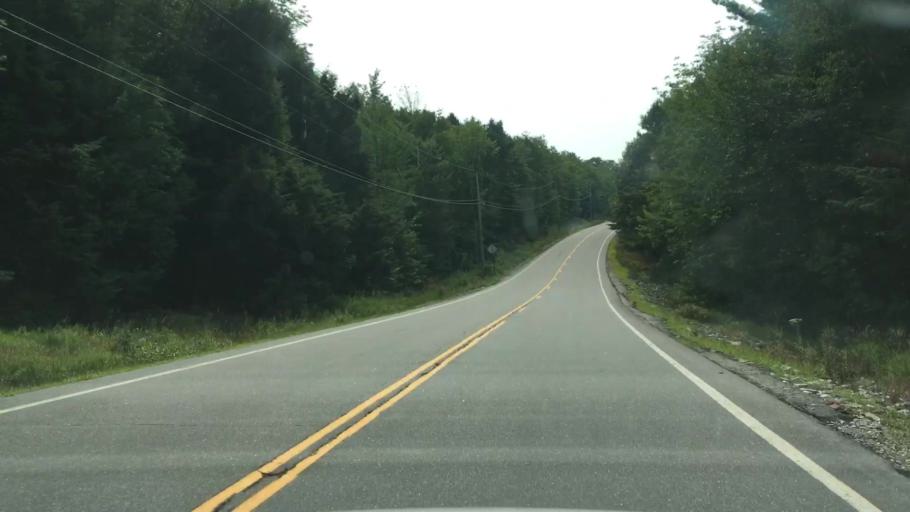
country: US
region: Maine
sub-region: Oxford County
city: Buckfield
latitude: 44.2652
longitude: -70.4253
